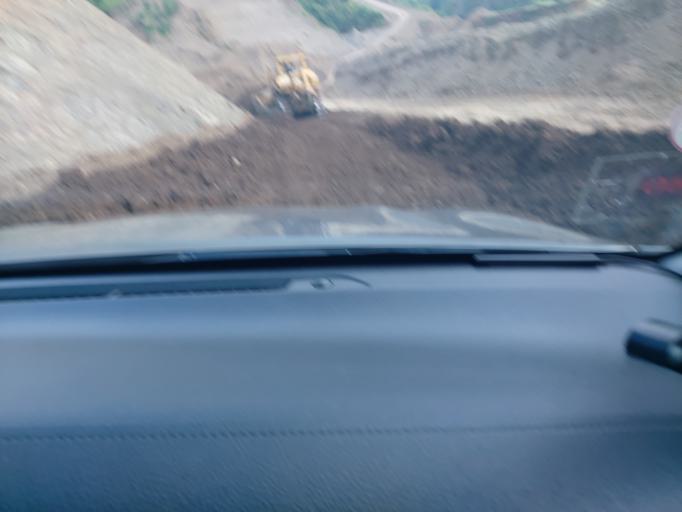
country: ET
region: Amhara
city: Debark'
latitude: 13.4022
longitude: 38.2159
